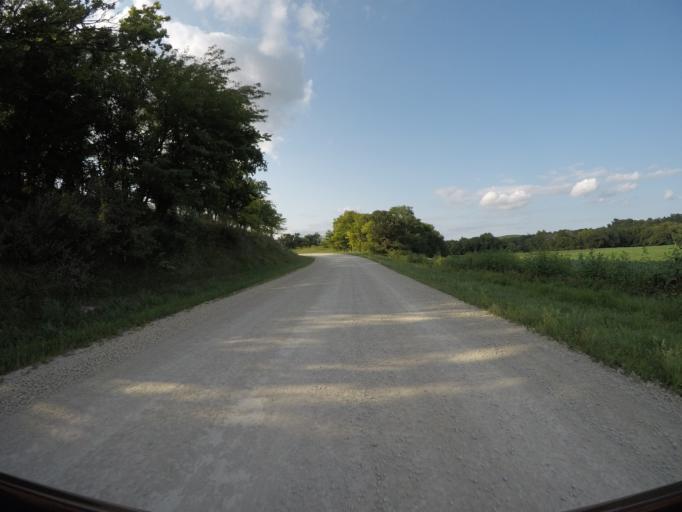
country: US
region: Kansas
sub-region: Wabaunsee County
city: Alma
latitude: 38.8871
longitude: -96.2090
